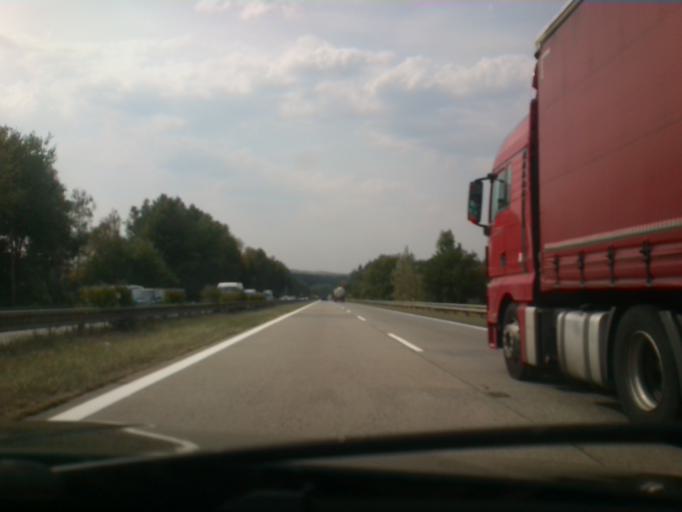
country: CZ
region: Central Bohemia
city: Divisov
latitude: 49.8053
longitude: 14.8983
